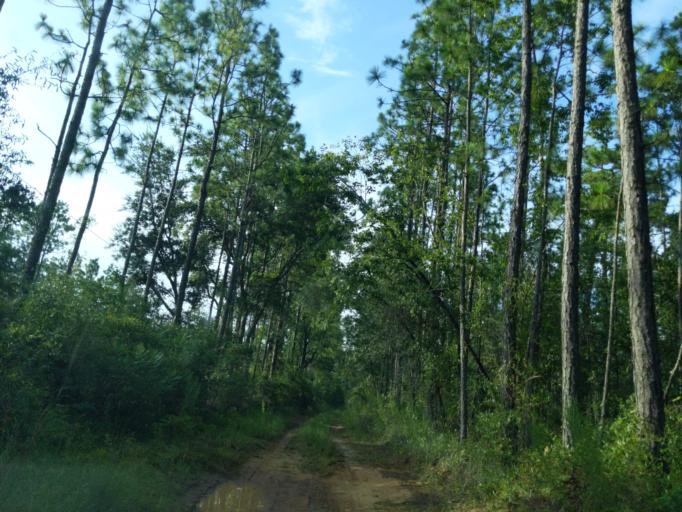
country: US
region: Florida
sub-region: Leon County
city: Tallahassee
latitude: 30.3561
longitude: -84.3611
